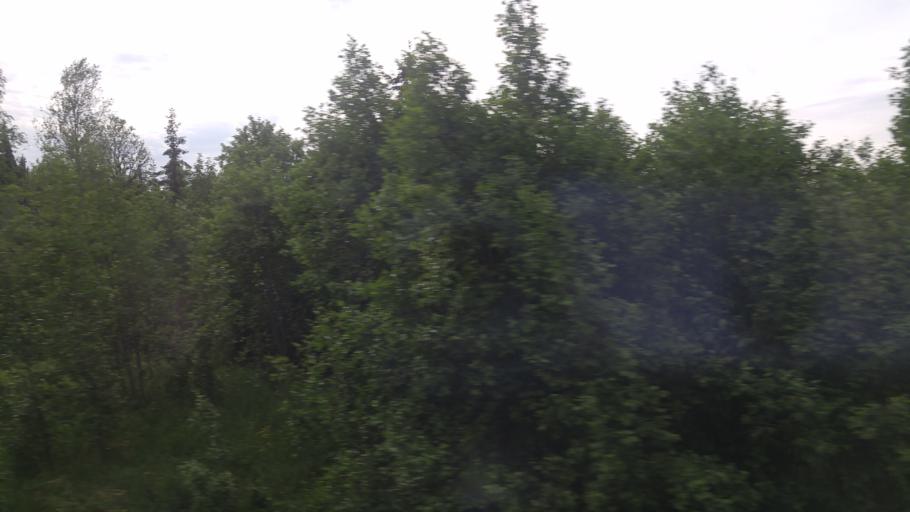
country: SE
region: Jaemtland
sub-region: Are Kommun
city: Are
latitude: 63.3892
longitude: 12.7878
